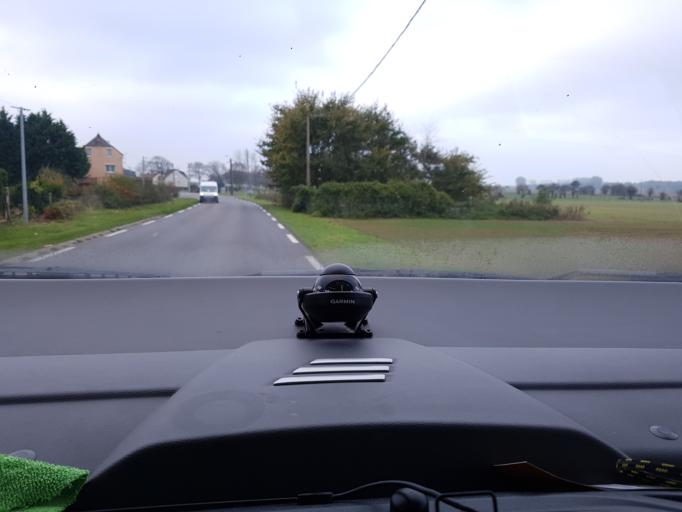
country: FR
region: Picardie
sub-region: Departement de la Somme
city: Ault
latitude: 50.0793
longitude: 1.4378
